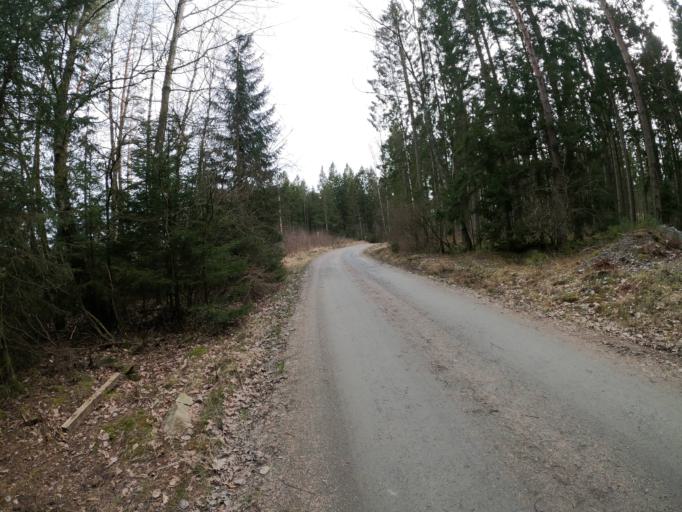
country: SE
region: Vaestra Goetaland
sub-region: Molndal
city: Kallered
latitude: 57.6201
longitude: 12.0787
